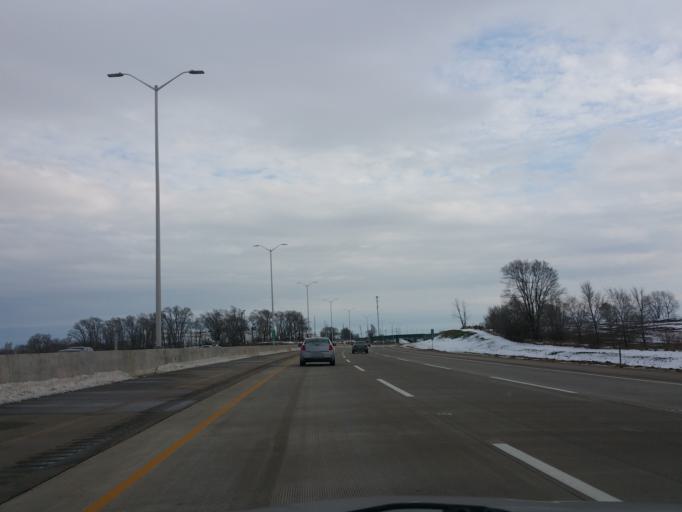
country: US
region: Illinois
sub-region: Winnebago County
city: Cherry Valley
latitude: 42.2453
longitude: -88.9270
